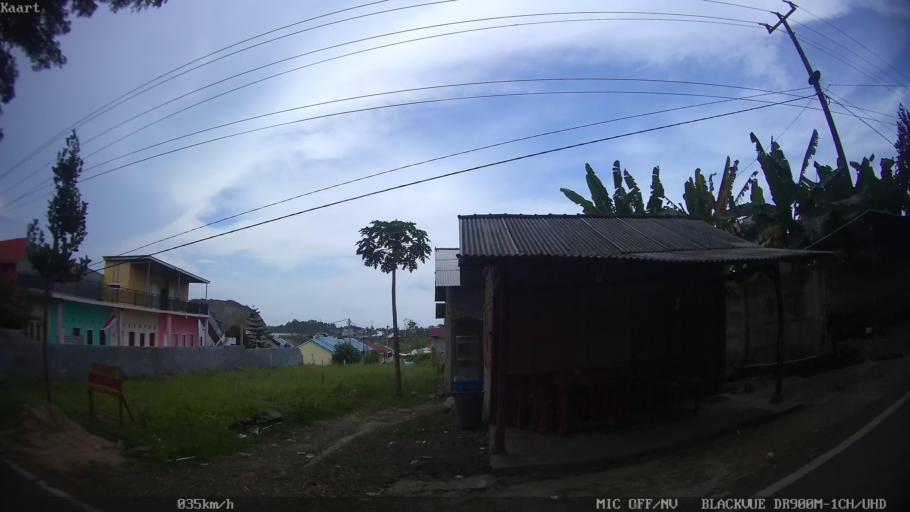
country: ID
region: Lampung
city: Bandarlampung
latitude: -5.4127
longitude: 105.1920
